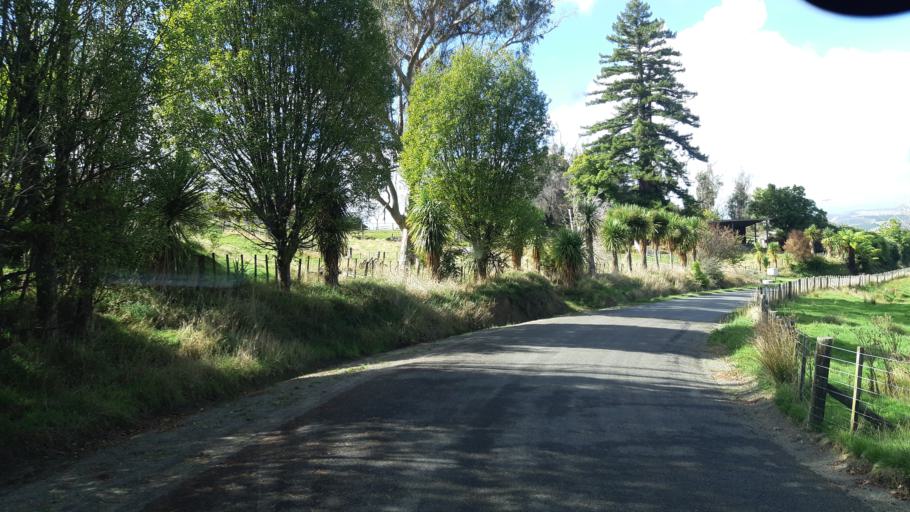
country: NZ
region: Manawatu-Wanganui
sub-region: Ruapehu District
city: Waiouru
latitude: -39.8578
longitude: 175.6554
